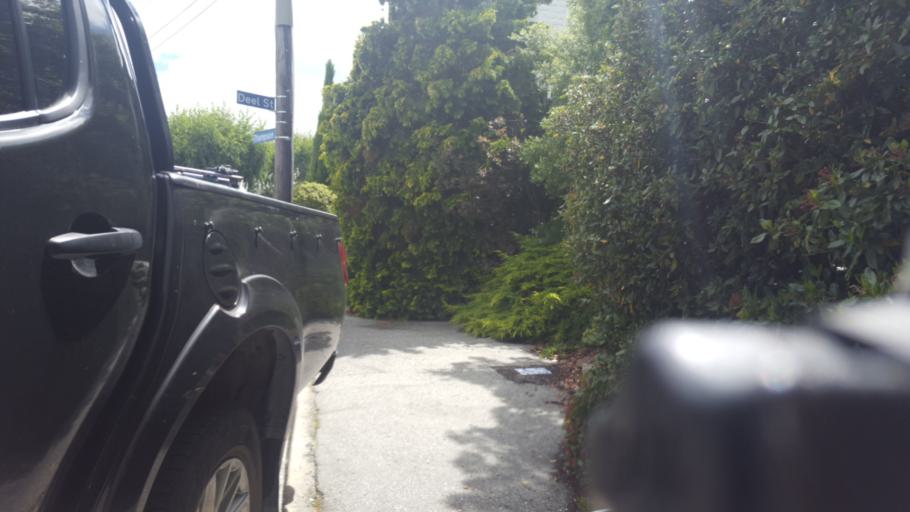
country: NZ
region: Otago
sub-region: Queenstown-Lakes District
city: Wanaka
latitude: -45.2571
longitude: 169.3944
